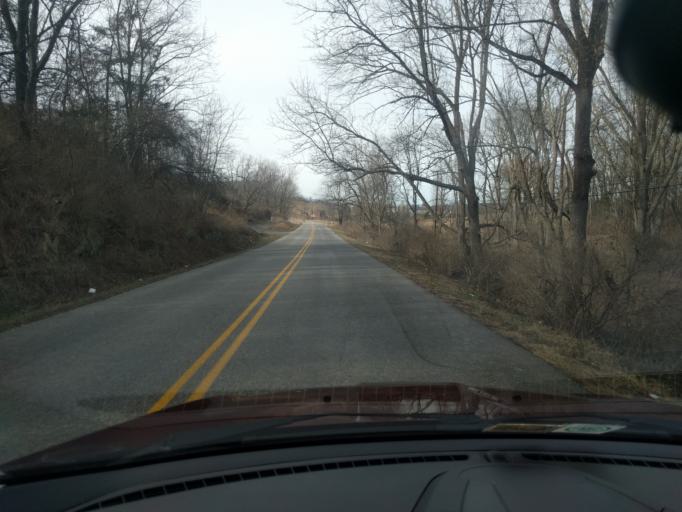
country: US
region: Virginia
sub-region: Augusta County
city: Stuarts Draft
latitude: 37.9282
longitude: -79.2084
